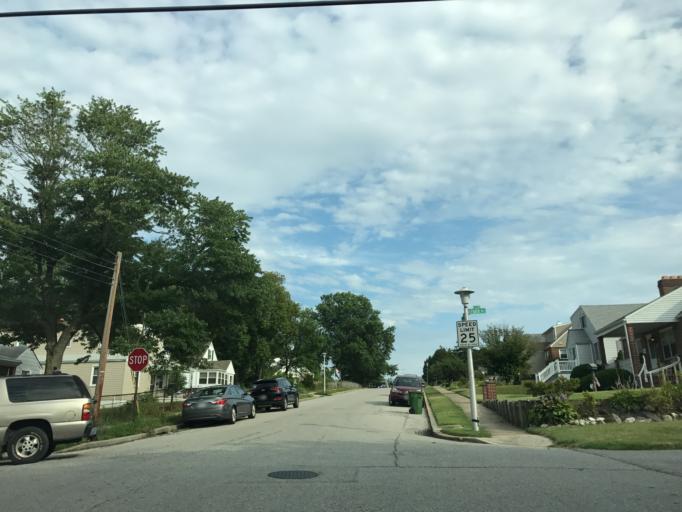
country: US
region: Maryland
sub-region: Baltimore County
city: Parkville
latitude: 39.3715
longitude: -76.5560
